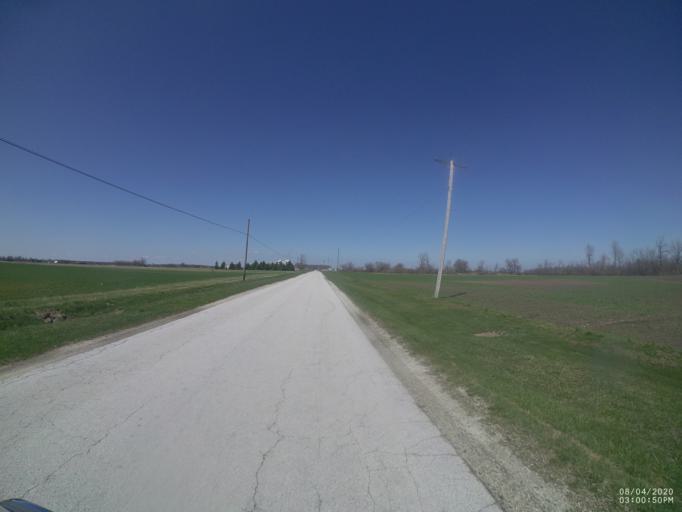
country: US
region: Ohio
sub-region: Sandusky County
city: Stony Prairie
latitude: 41.3286
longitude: -83.2398
